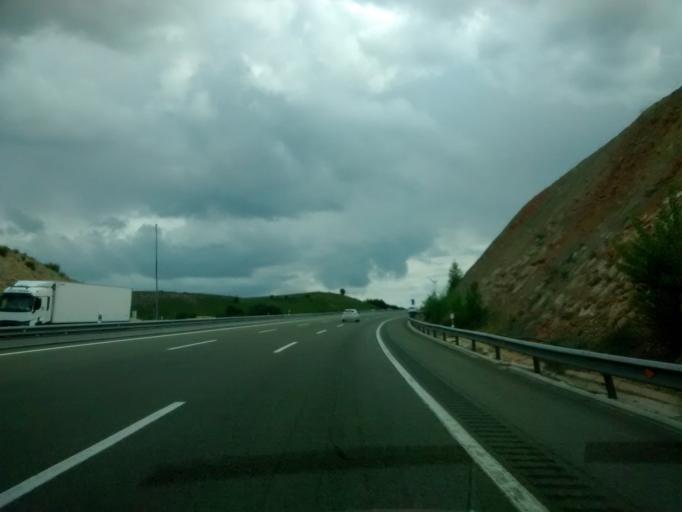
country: ES
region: Castille-La Mancha
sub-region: Provincia de Guadalajara
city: Alcolea del Pinar
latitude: 41.1021
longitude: -2.4502
